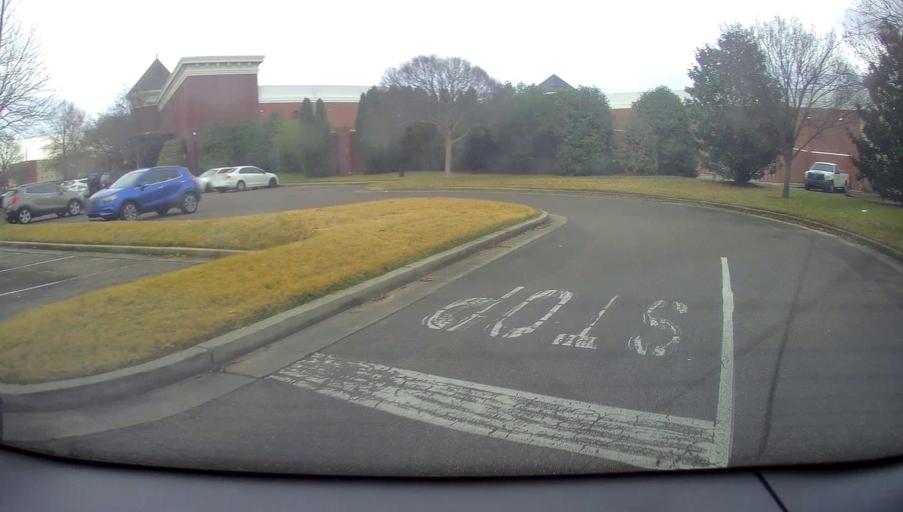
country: US
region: Tennessee
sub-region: Shelby County
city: Collierville
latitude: 35.0236
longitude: -89.7215
